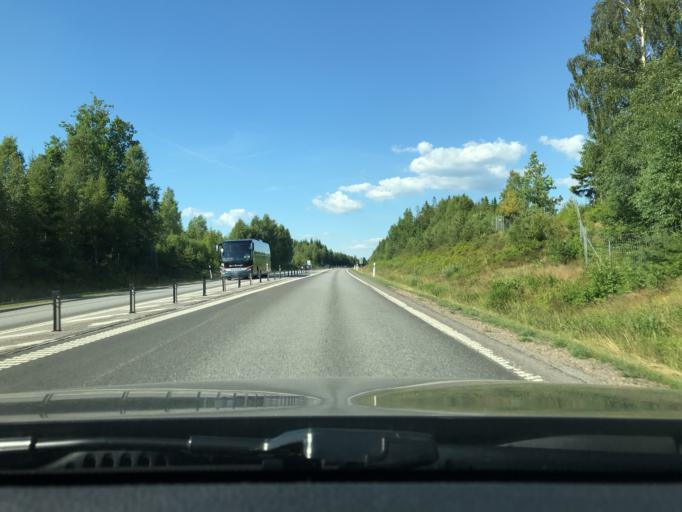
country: SE
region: Skane
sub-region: Osby Kommun
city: Osby
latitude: 56.4313
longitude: 14.0600
